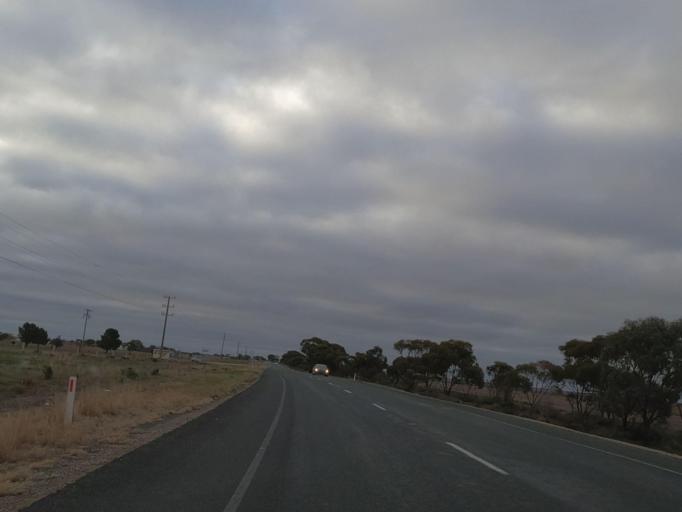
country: AU
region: Victoria
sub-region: Swan Hill
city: Swan Hill
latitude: -35.5838
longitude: 143.7901
